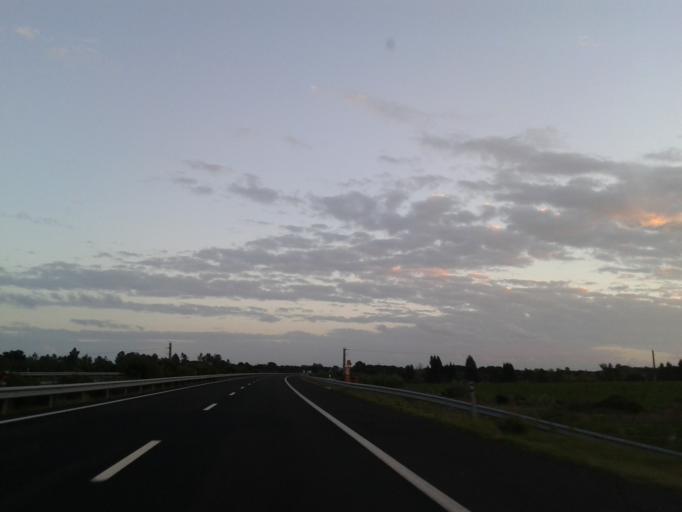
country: PT
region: Evora
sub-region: Vendas Novas
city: Vendas Novas
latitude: 38.6975
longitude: -8.6395
